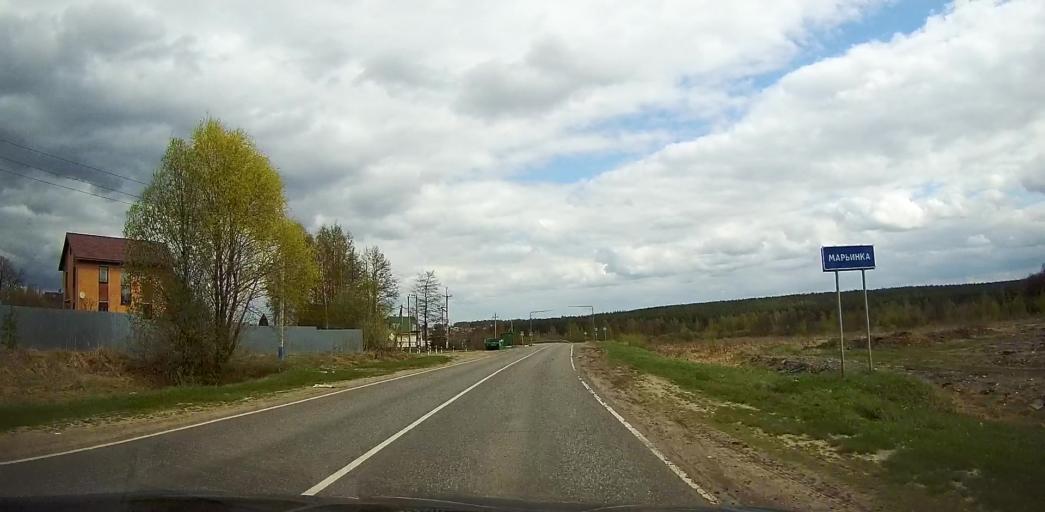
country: RU
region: Moskovskaya
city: Imeni Tsyurupy
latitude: 55.4841
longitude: 38.6159
